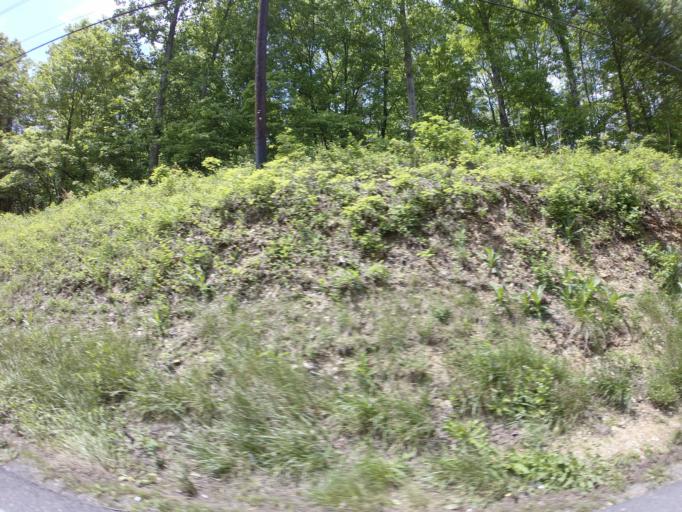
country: US
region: Maryland
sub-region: Frederick County
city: Urbana
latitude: 39.3506
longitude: -77.3769
